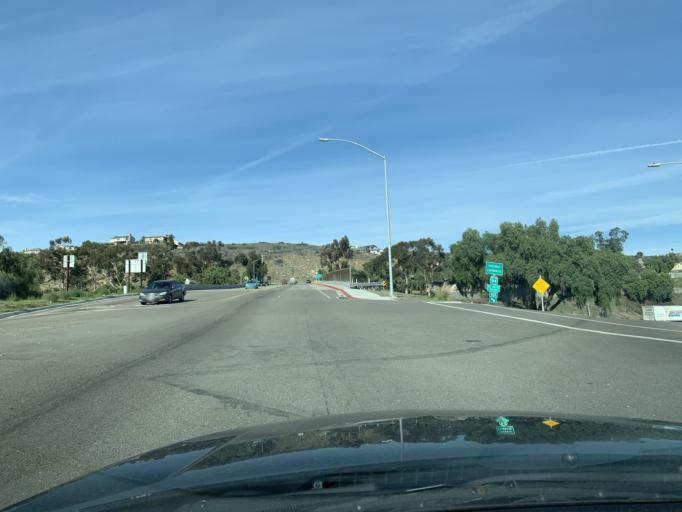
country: US
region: California
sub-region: San Diego County
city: Lemon Grove
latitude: 32.7455
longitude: -117.0310
